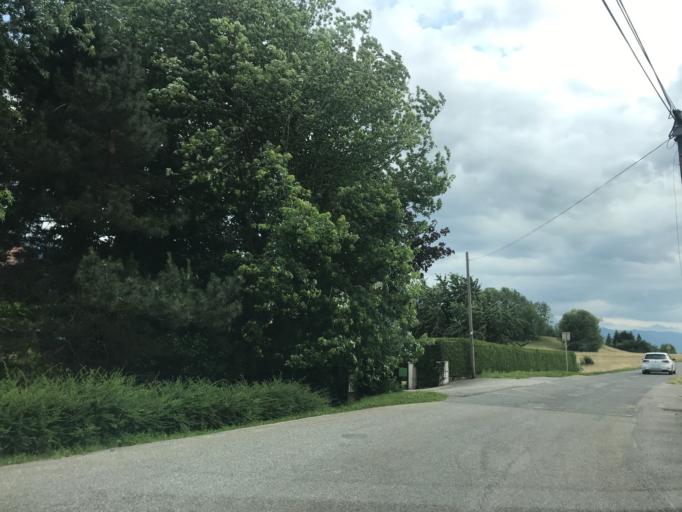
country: FR
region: Rhone-Alpes
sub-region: Departement de la Savoie
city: Mercury
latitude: 45.6786
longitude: 6.3411
